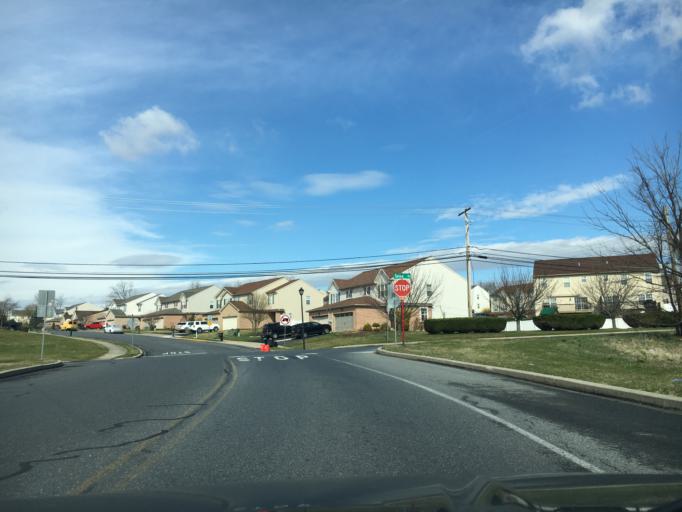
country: US
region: Pennsylvania
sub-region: Northampton County
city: North Catasauqua
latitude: 40.6847
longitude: -75.4698
